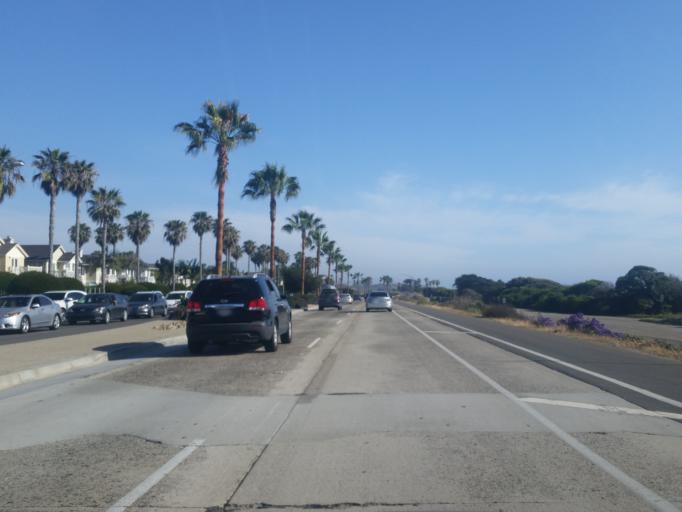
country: US
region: California
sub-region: San Diego County
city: Carlsbad
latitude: 33.1013
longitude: -117.3181
